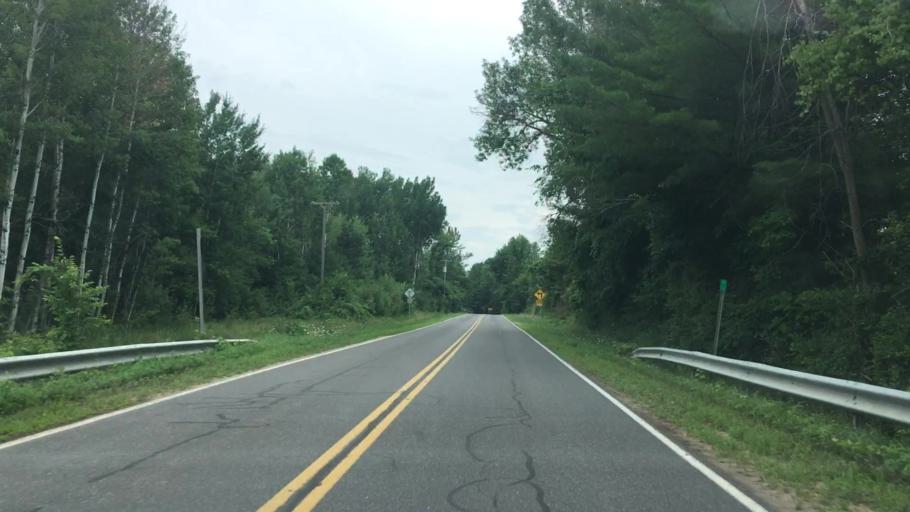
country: US
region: New York
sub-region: Clinton County
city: Peru
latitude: 44.5285
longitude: -73.5736
